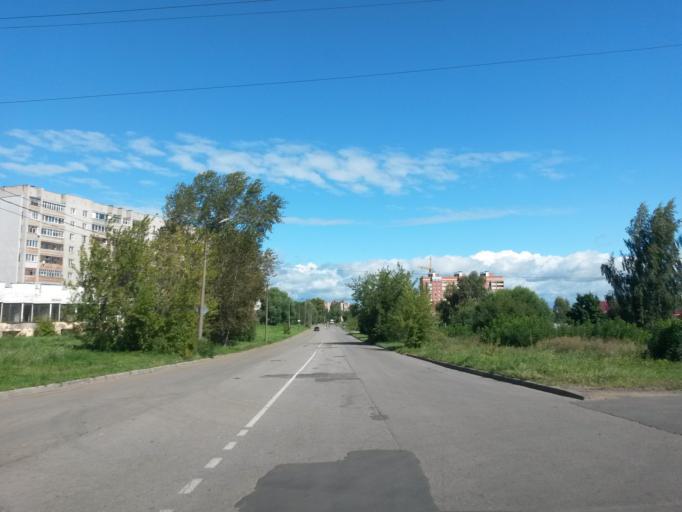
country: RU
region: Jaroslavl
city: Yaroslavl
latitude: 57.5829
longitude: 39.8658
